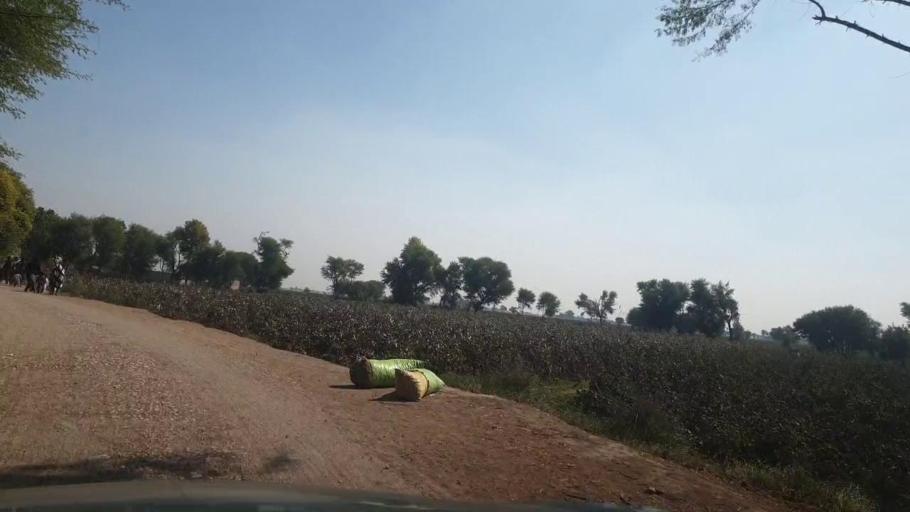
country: PK
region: Sindh
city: Bhan
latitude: 26.5770
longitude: 67.6747
